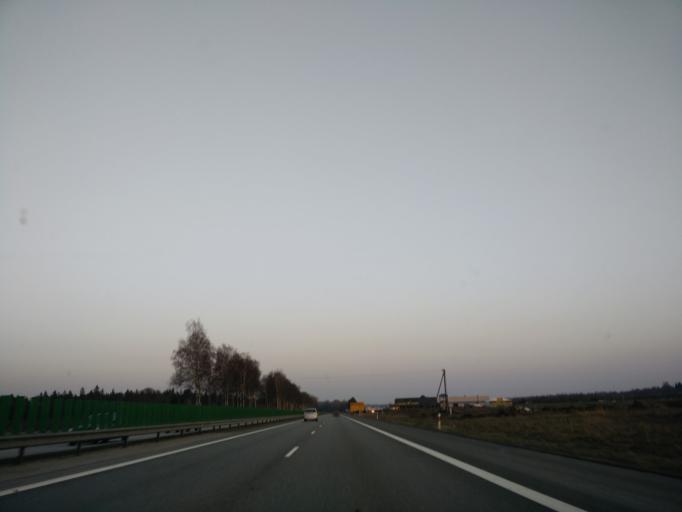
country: LT
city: Lentvaris
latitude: 54.7055
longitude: 25.0011
